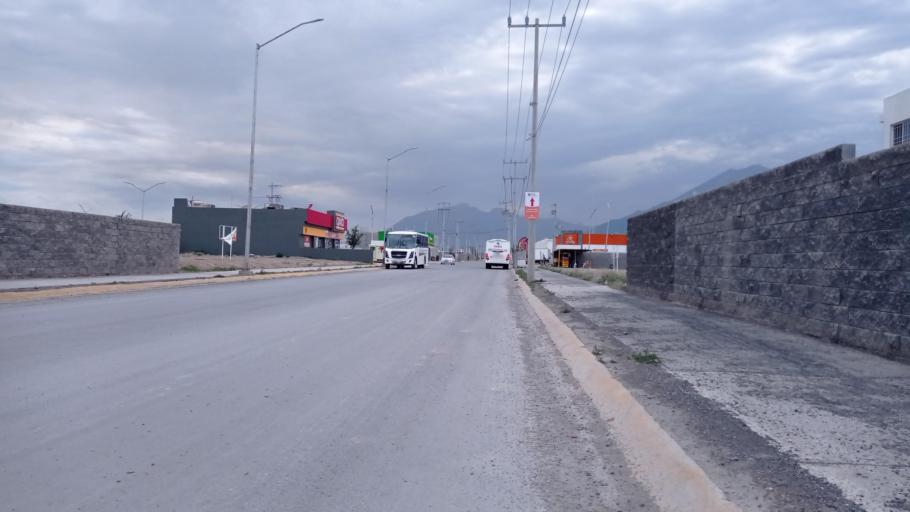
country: MX
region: Nuevo Leon
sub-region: Salinas Victoria
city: Simeprodeso (Colectivo Nuevo)
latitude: 25.8772
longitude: -100.3159
